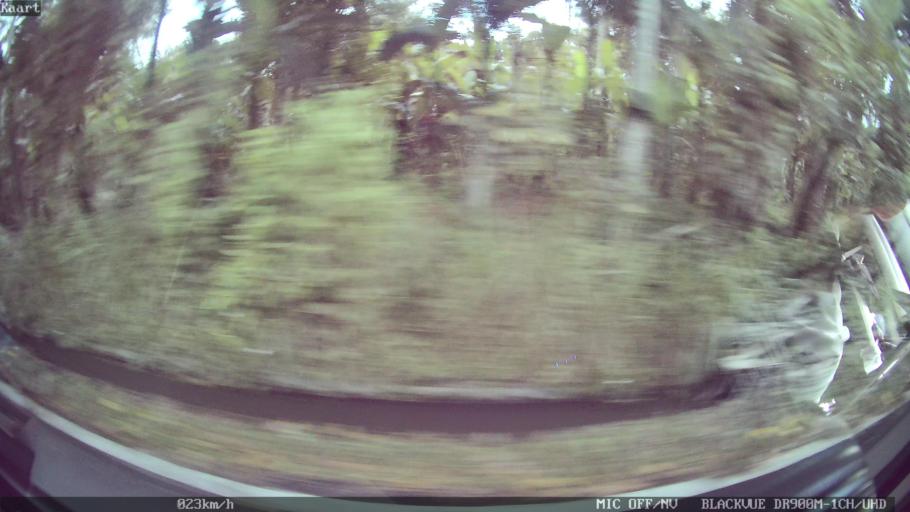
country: ID
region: Bali
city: Pemijian
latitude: -8.4515
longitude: 115.2289
